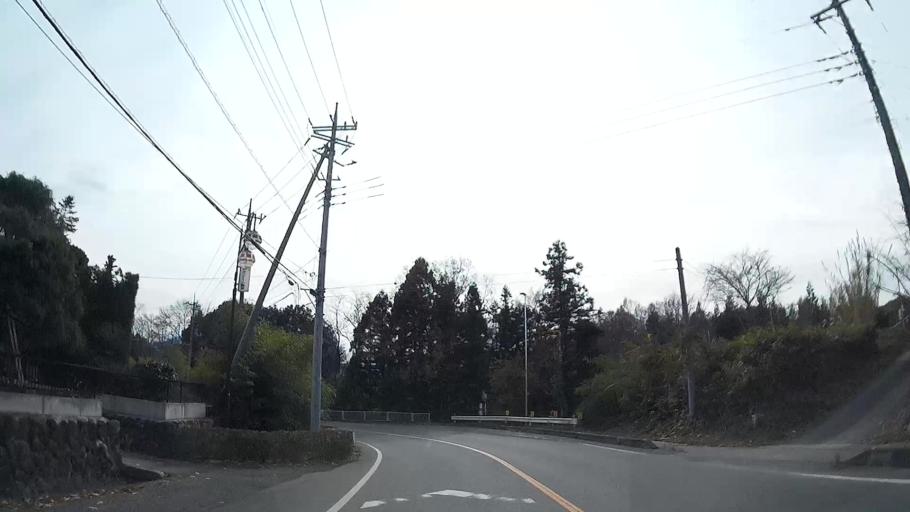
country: JP
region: Saitama
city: Chichibu
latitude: 36.0274
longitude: 139.0380
